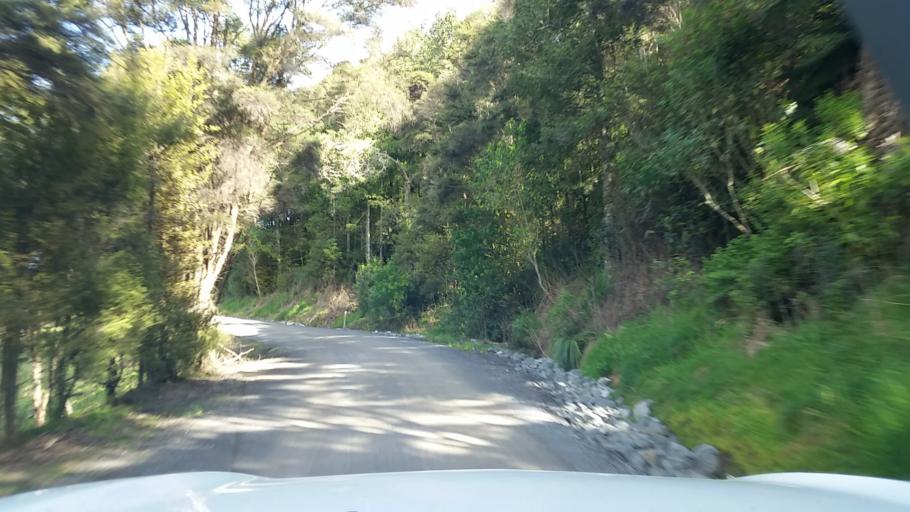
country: NZ
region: Waikato
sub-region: Hauraki District
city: Ngatea
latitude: -37.4473
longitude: 175.4843
